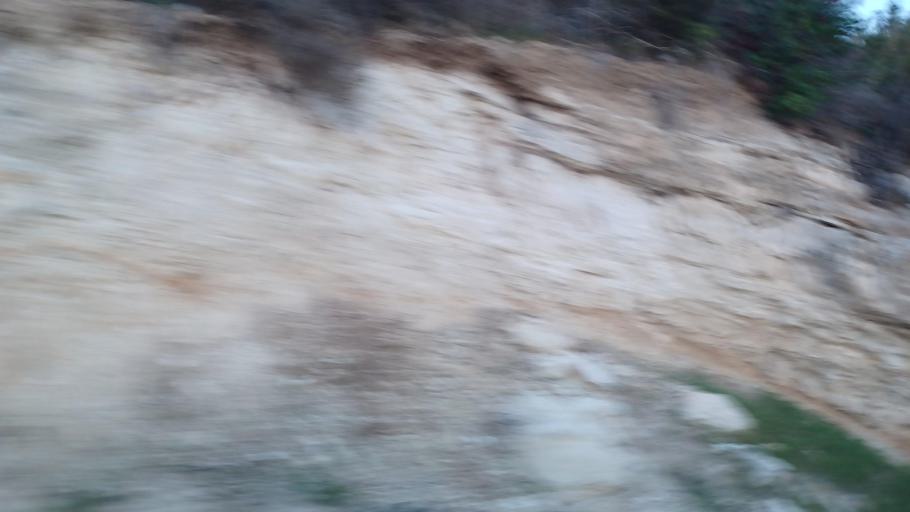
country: CY
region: Pafos
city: Polis
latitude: 34.9871
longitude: 32.4388
